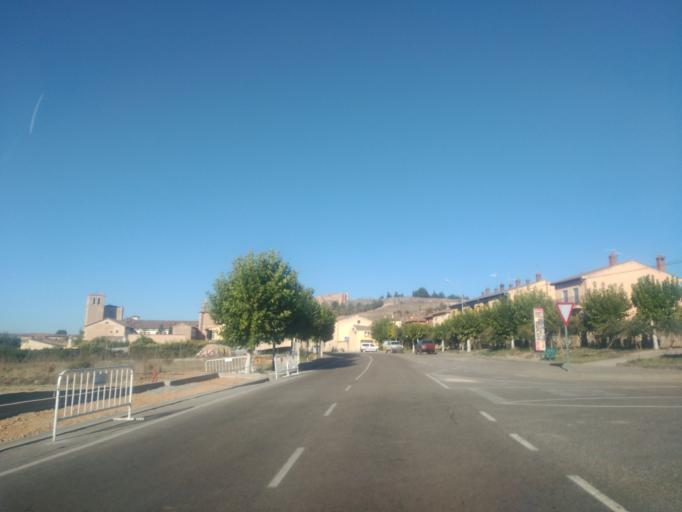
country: ES
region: Castille and Leon
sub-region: Provincia de Burgos
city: Penaranda de Duero
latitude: 41.6898
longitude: -3.4742
